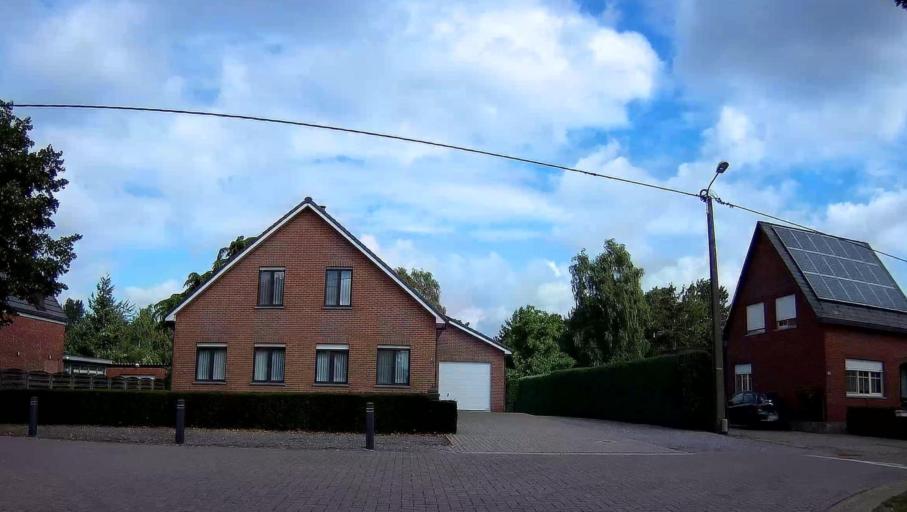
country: BE
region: Flanders
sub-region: Provincie Antwerpen
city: Balen
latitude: 51.2225
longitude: 5.2054
